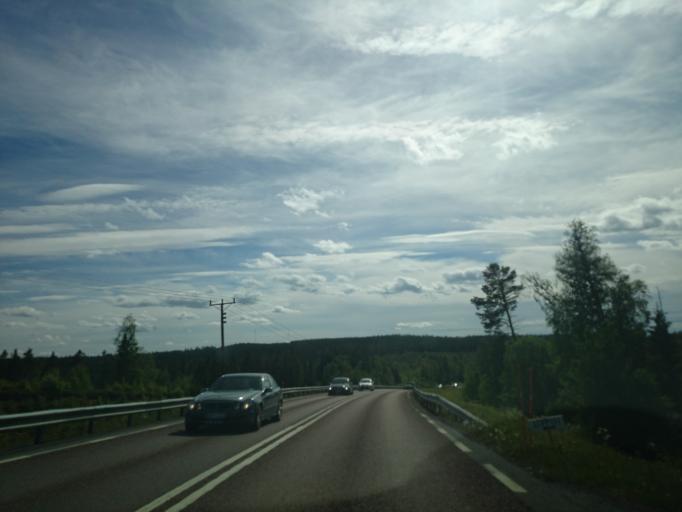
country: SE
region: Jaemtland
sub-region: Krokoms Kommun
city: Valla
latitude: 63.3323
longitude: 13.9745
